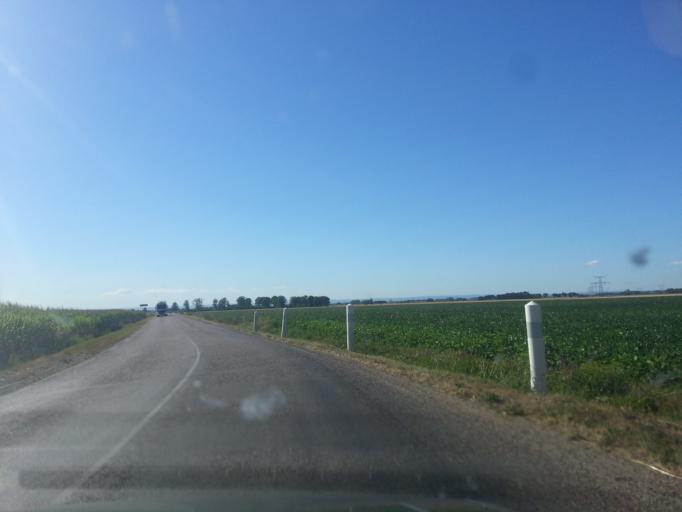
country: FR
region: Bourgogne
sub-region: Departement de Saone-et-Loire
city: Saint-Martin-en-Bresse
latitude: 46.8513
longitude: 5.0771
